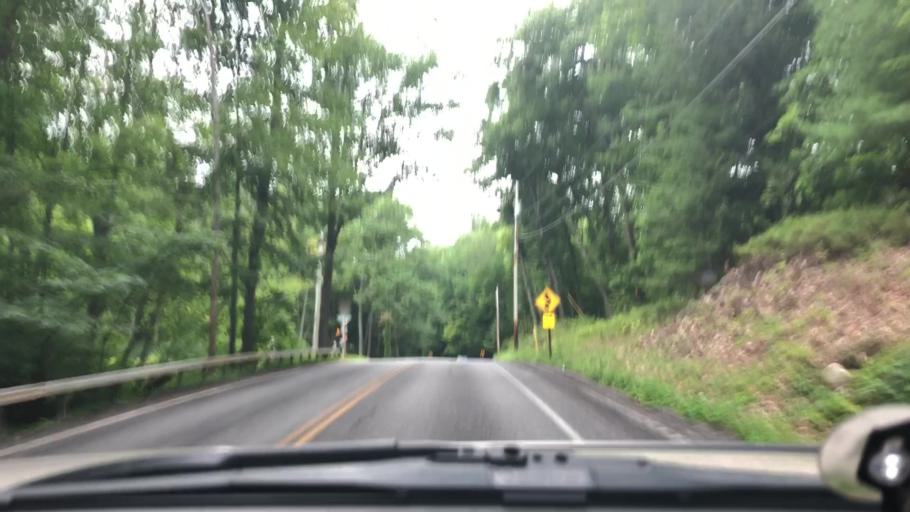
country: US
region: New York
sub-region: Saratoga County
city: Corinth
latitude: 43.1937
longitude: -73.7558
